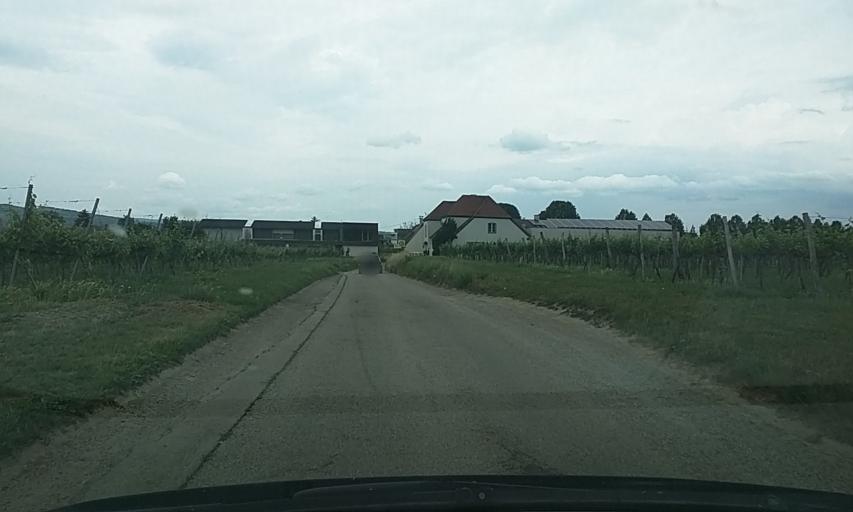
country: AT
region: Lower Austria
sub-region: Politischer Bezirk Krems
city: Weinzierl bei Krems
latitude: 48.3816
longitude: 15.6149
